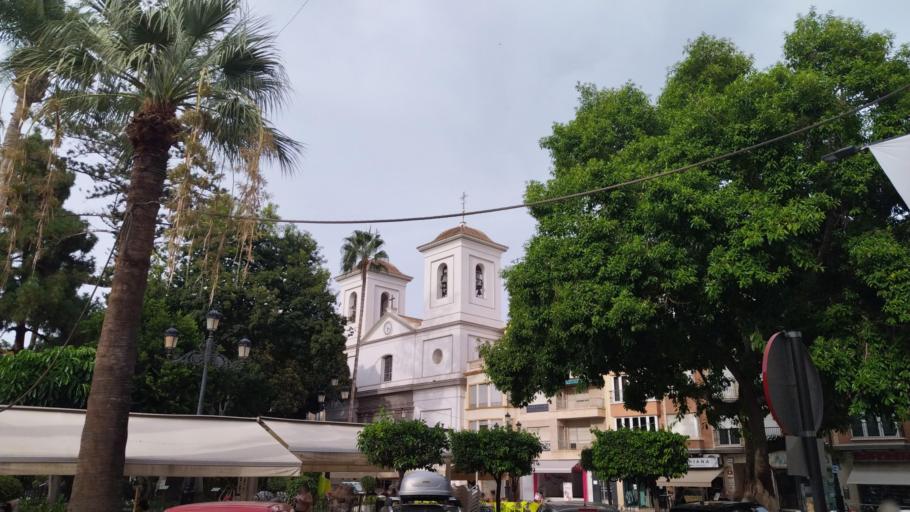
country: ES
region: Murcia
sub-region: Murcia
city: Aguilas
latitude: 37.4038
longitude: -1.5817
